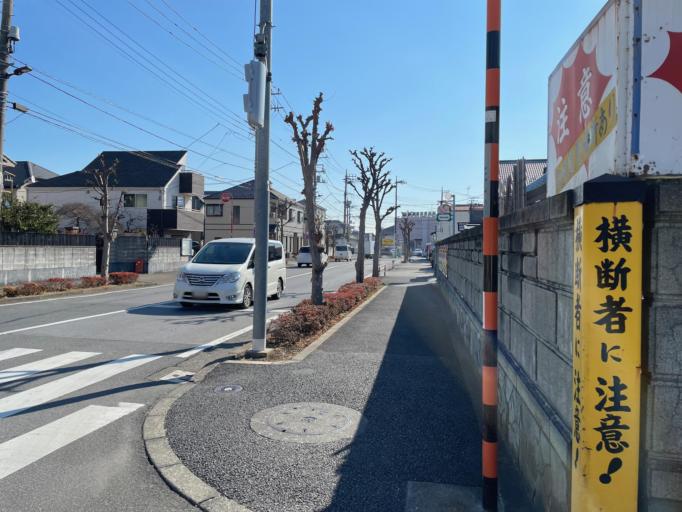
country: JP
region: Saitama
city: Soka
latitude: 35.7947
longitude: 139.7826
